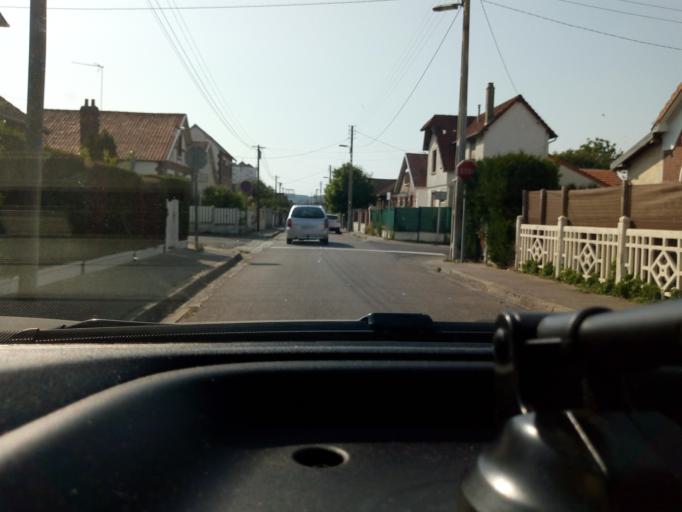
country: FR
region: Haute-Normandie
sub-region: Departement de la Seine-Maritime
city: Le Petit-Quevilly
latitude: 49.4072
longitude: 1.0607
